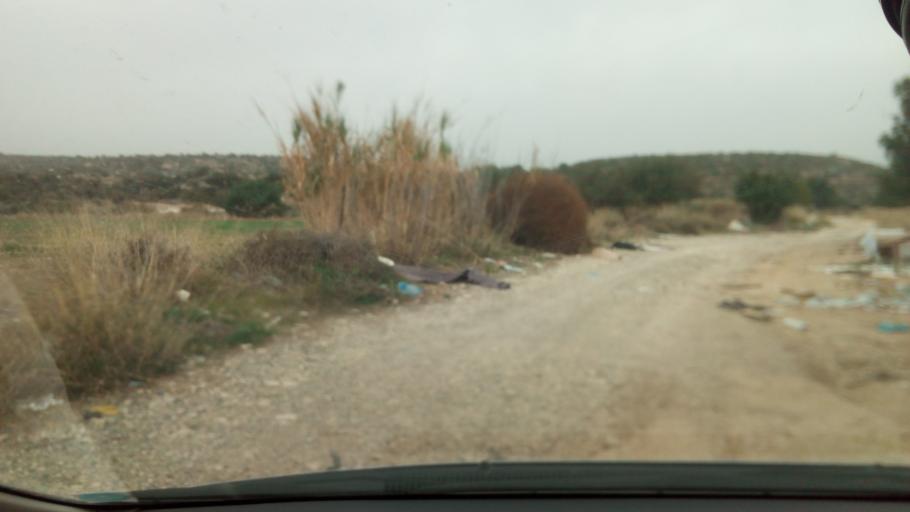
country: CY
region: Limassol
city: Ypsonas
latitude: 34.7082
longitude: 32.9567
